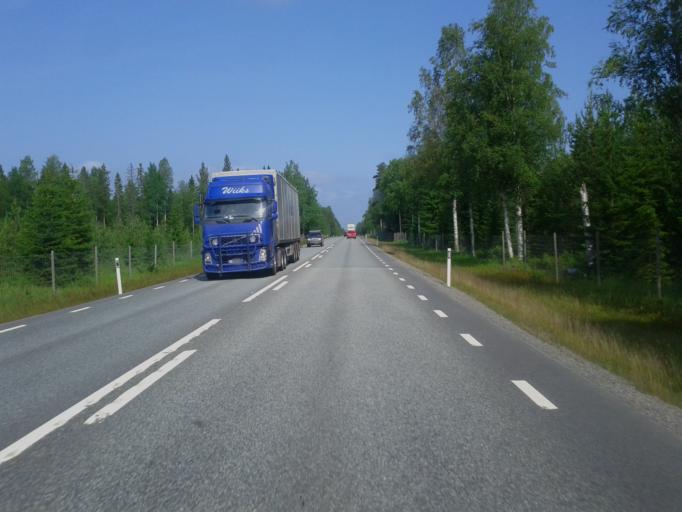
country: SE
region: Vaesterbotten
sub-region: Skelleftea Kommun
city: Burea
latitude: 64.5700
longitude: 21.2264
